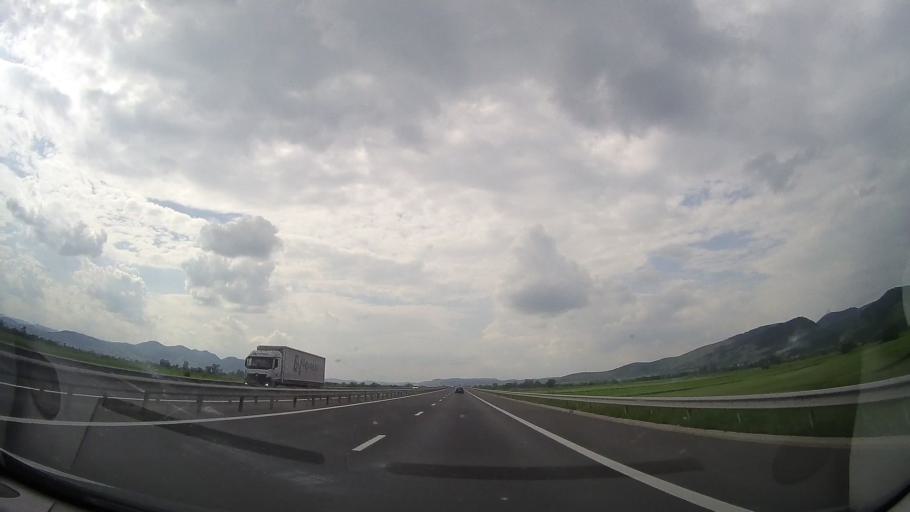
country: RO
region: Hunedoara
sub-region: Oras Simeria
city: Simeria
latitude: 45.8781
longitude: 23.0001
